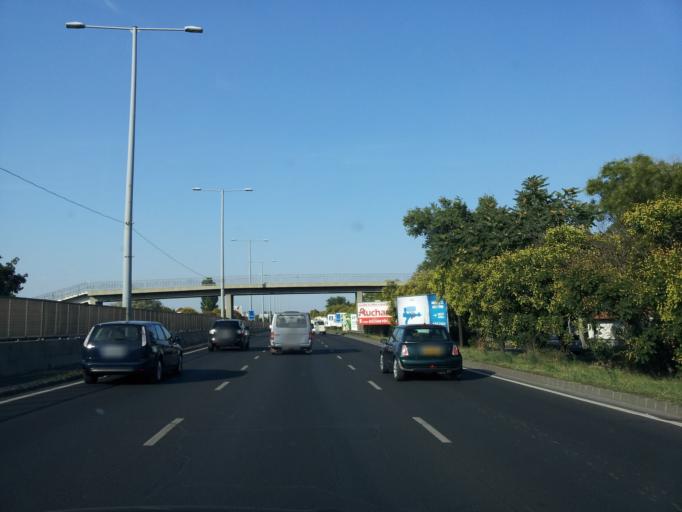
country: HU
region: Budapest
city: Budapest XV. keruelet
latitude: 47.5507
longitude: 19.1240
